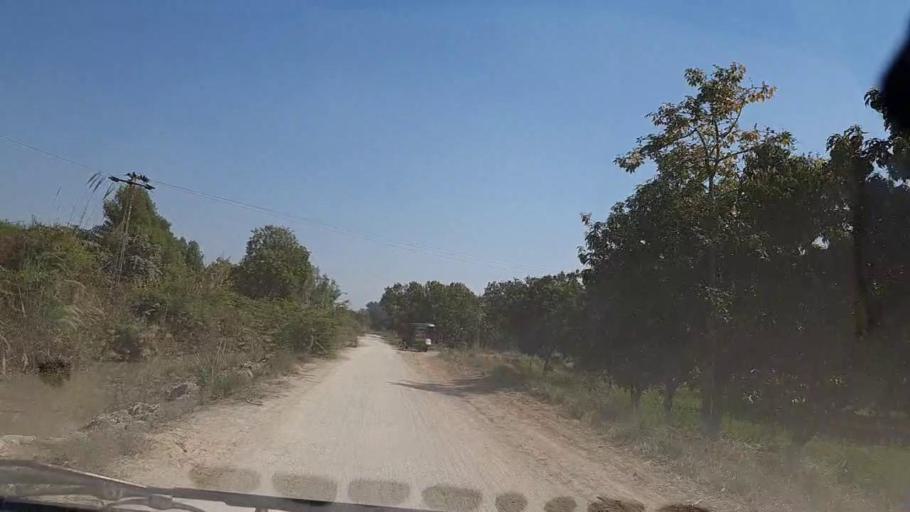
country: PK
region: Sindh
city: Mirpur Khas
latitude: 25.4707
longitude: 69.0368
